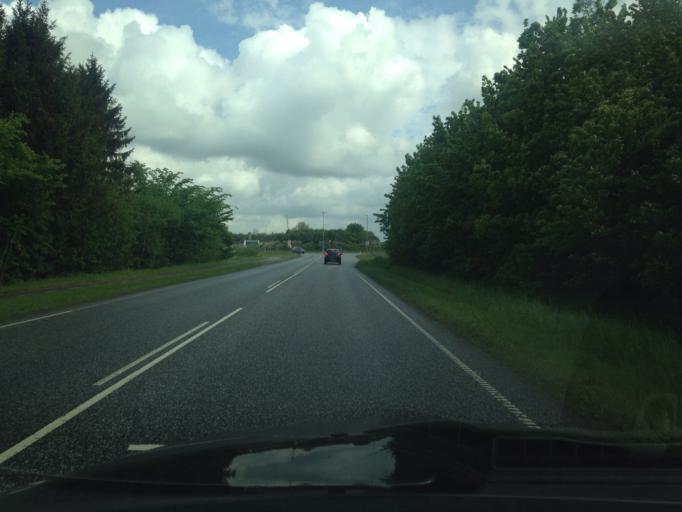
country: DK
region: South Denmark
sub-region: Kolding Kommune
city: Kolding
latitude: 55.5428
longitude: 9.4758
